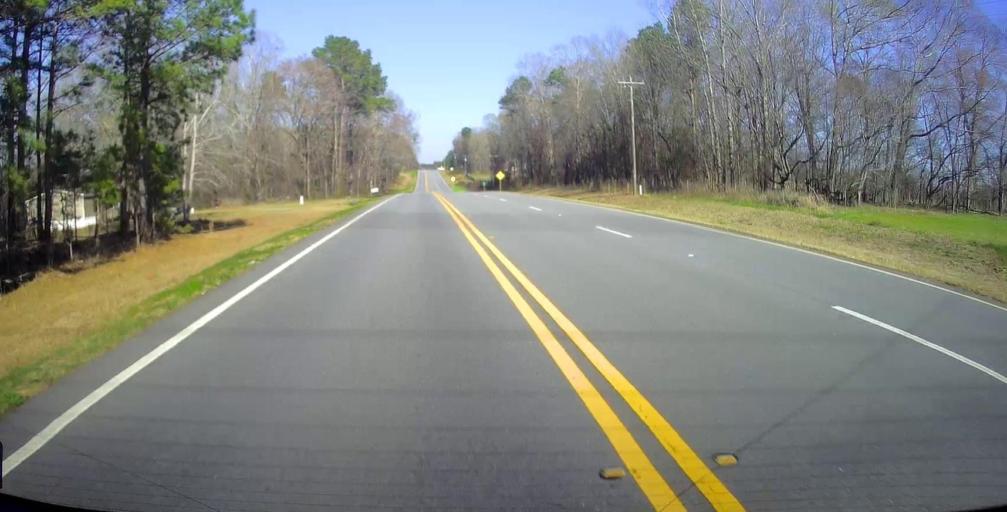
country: US
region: Georgia
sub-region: Macon County
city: Marshallville
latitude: 32.3306
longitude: -83.8675
